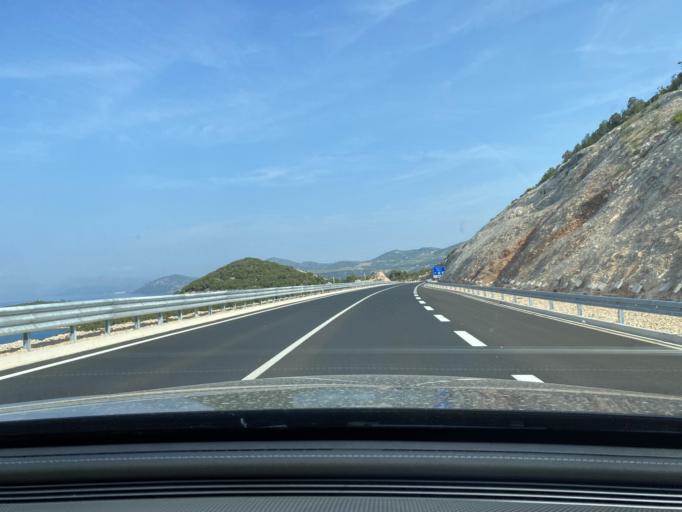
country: BA
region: Federation of Bosnia and Herzegovina
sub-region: Hercegovacko-Bosanski Kanton
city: Neum
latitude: 42.9140
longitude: 17.5280
